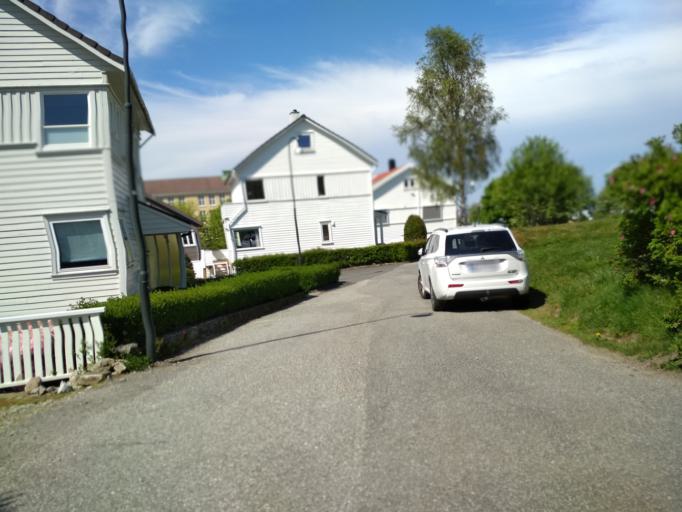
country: NO
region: Rogaland
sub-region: Stavanger
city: Stavanger
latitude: 58.9710
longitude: 5.7180
